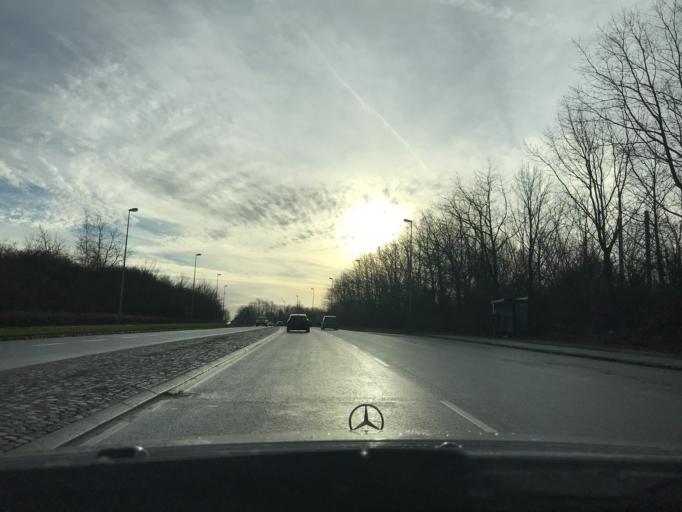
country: DK
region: South Denmark
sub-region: Sonderborg Kommune
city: Sonderborg
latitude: 54.9218
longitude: 9.7834
